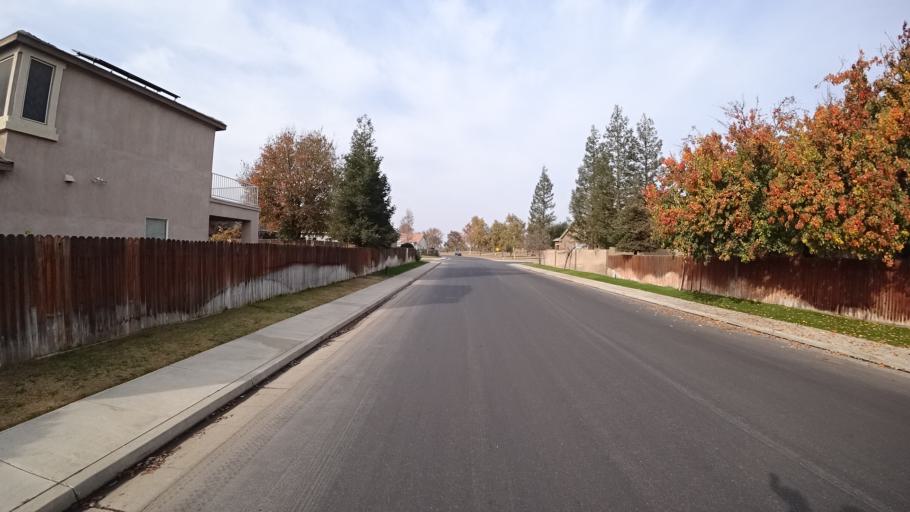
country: US
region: California
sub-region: Kern County
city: Rosedale
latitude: 35.3429
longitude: -119.1426
